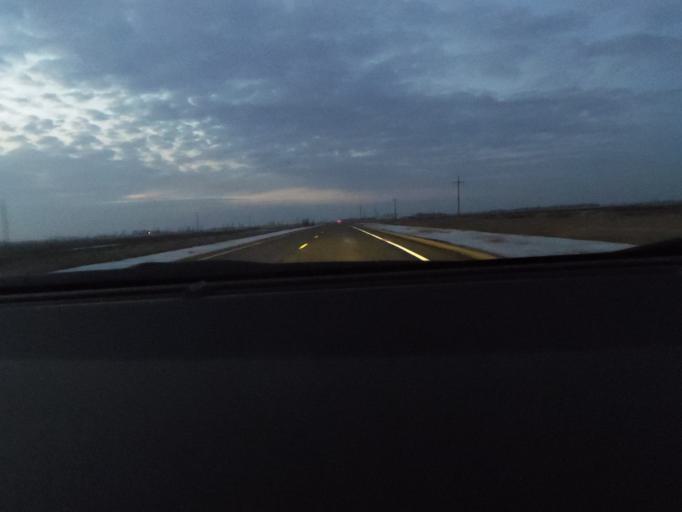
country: US
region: North Dakota
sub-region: Walsh County
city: Park River
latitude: 48.2037
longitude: -97.6226
